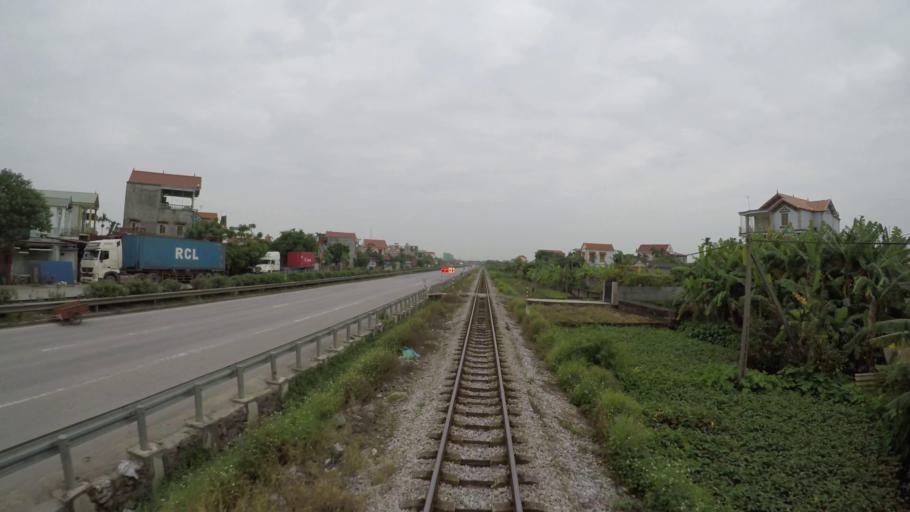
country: VN
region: Hai Duong
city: Phu Thai
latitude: 20.9581
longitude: 106.5243
